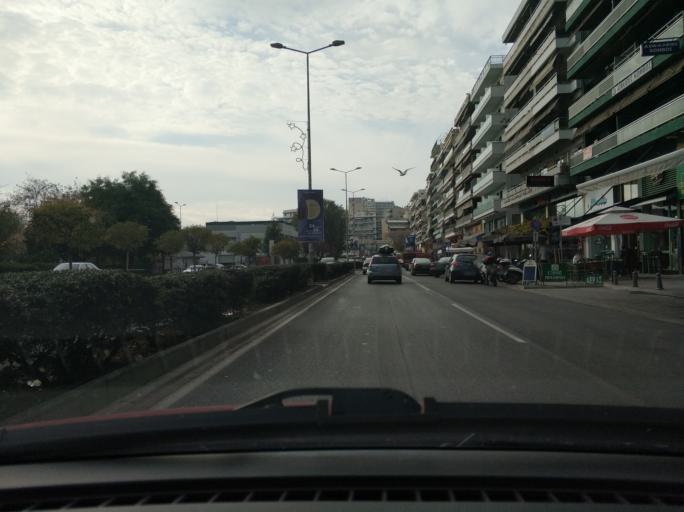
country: GR
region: East Macedonia and Thrace
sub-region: Nomos Kavalas
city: Kavala
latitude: 40.9363
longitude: 24.4050
